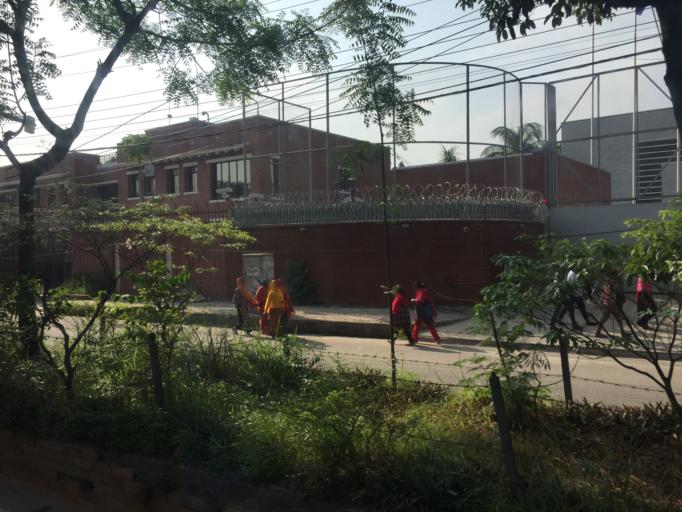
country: BD
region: Dhaka
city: Paltan
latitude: 23.7974
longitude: 90.4222
